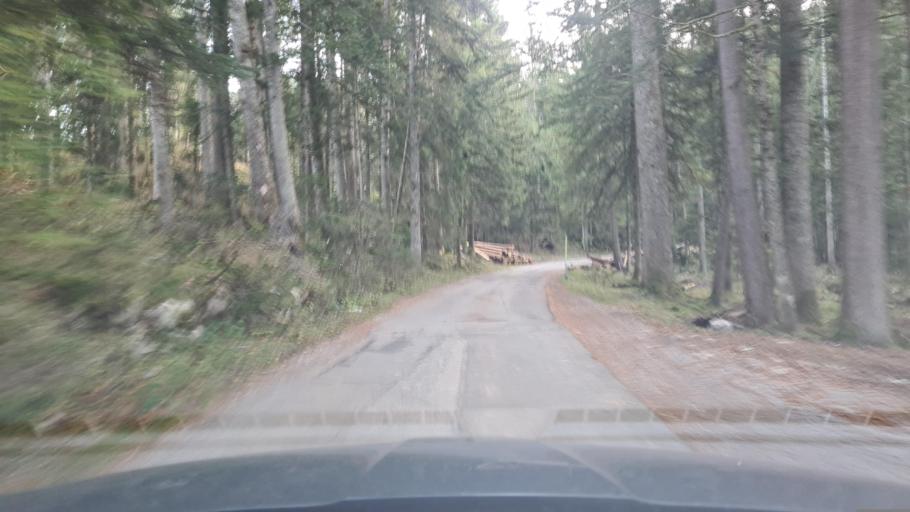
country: AT
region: Salzburg
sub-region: Politischer Bezirk Hallein
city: Scheffau am Tennengebirge
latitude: 47.6368
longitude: 13.2302
